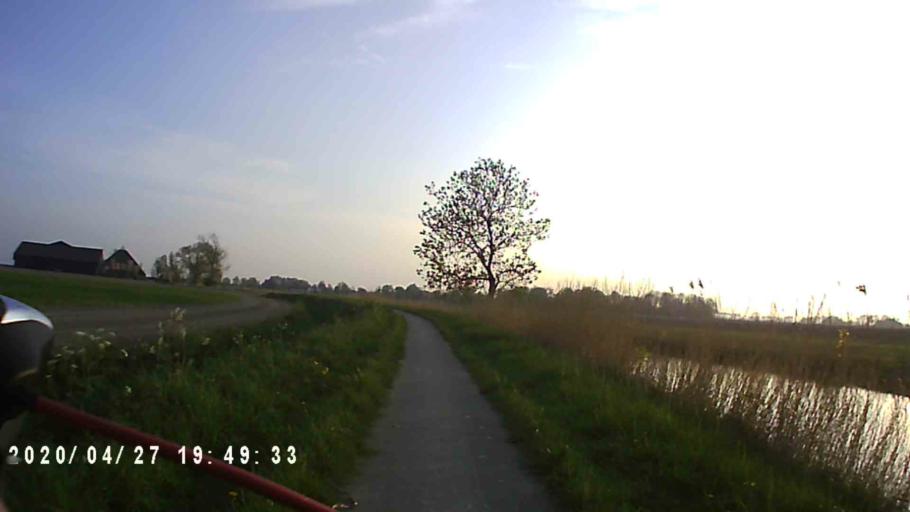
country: NL
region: Groningen
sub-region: Gemeente Zuidhorn
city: Oldehove
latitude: 53.3452
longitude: 6.4336
